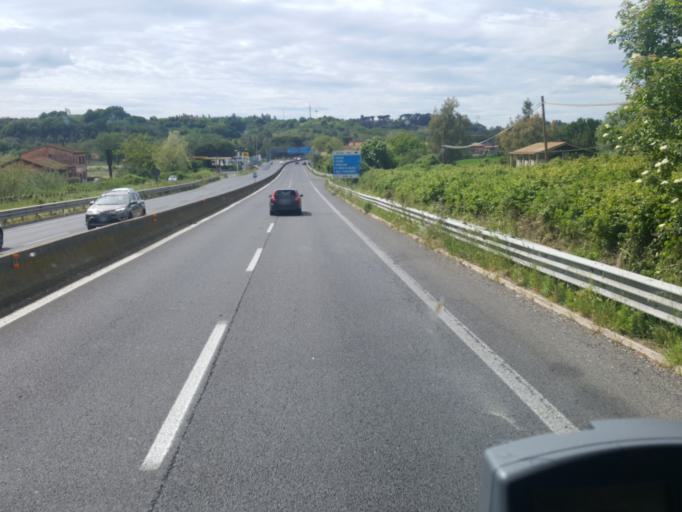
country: IT
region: Latium
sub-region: Citta metropolitana di Roma Capitale
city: Ara Nova
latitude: 41.9055
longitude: 12.2687
